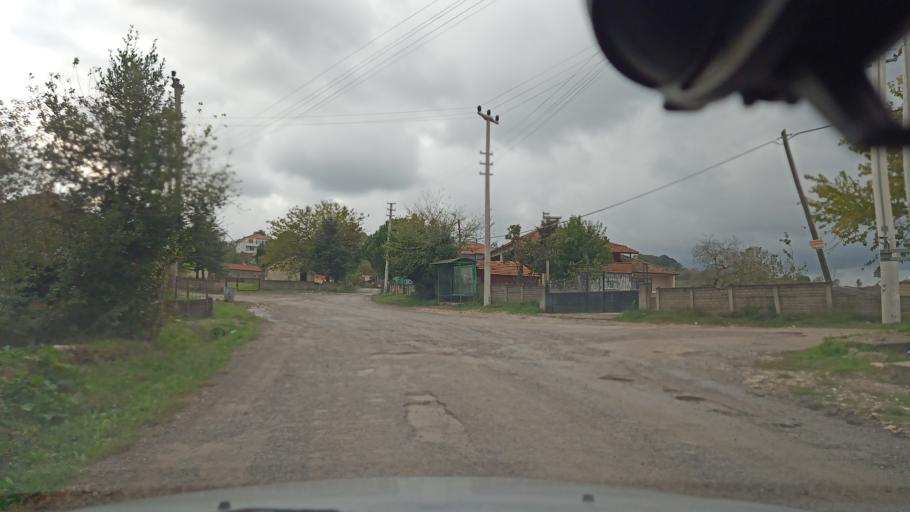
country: TR
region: Sakarya
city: Karasu
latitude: 41.0883
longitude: 30.5867
